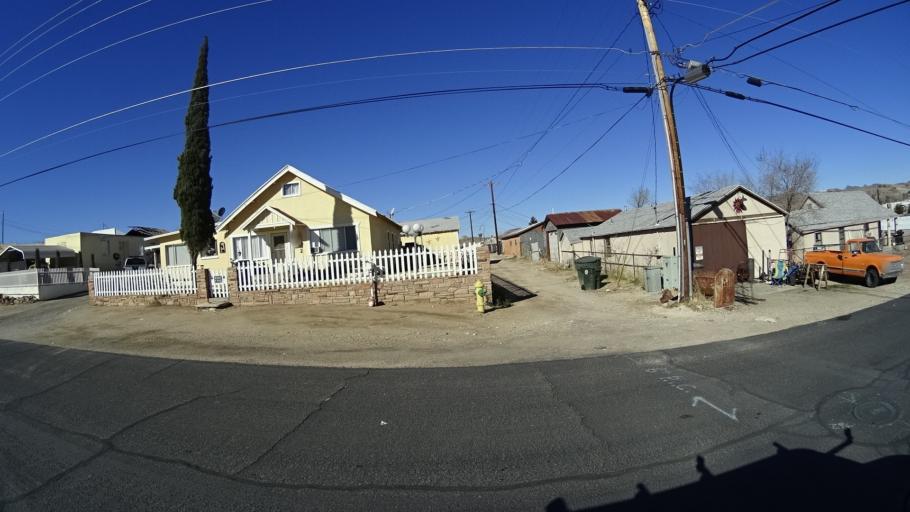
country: US
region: Arizona
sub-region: Mohave County
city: Kingman
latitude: 35.1874
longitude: -114.0548
